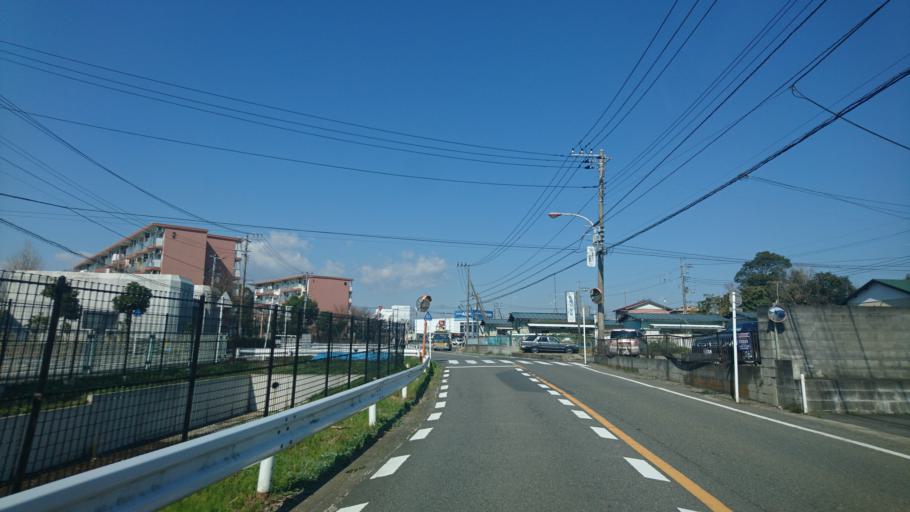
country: JP
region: Kanagawa
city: Fujisawa
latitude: 35.4016
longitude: 139.4437
